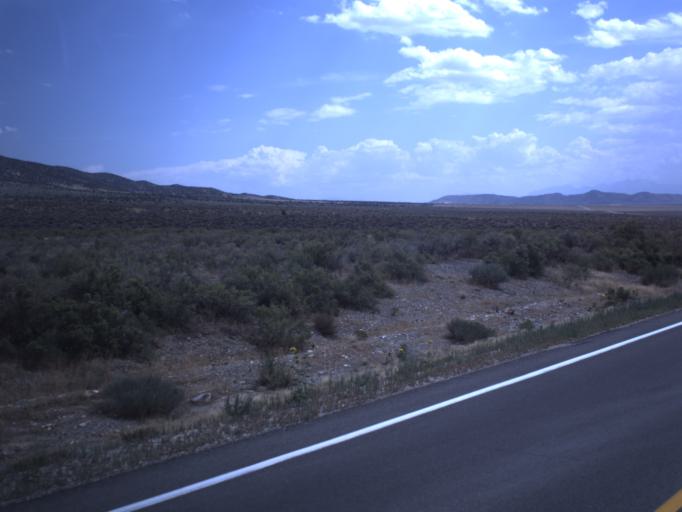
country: US
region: Utah
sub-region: Tooele County
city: Tooele
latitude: 40.2958
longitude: -112.2741
